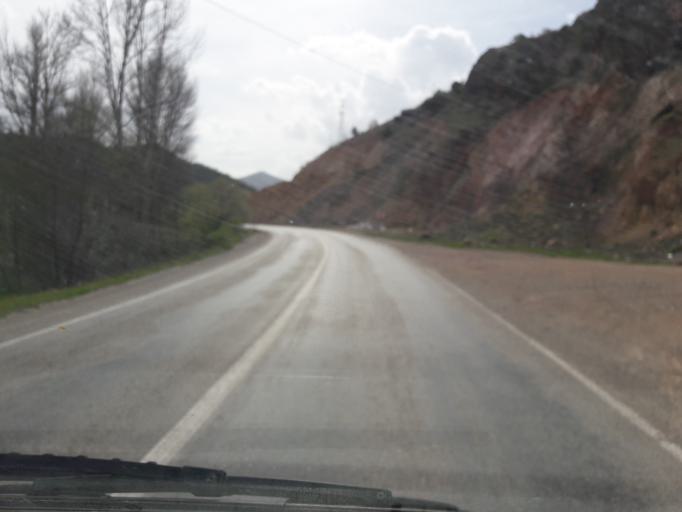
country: TR
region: Gumushane
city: Kale
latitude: 40.3960
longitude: 39.5980
